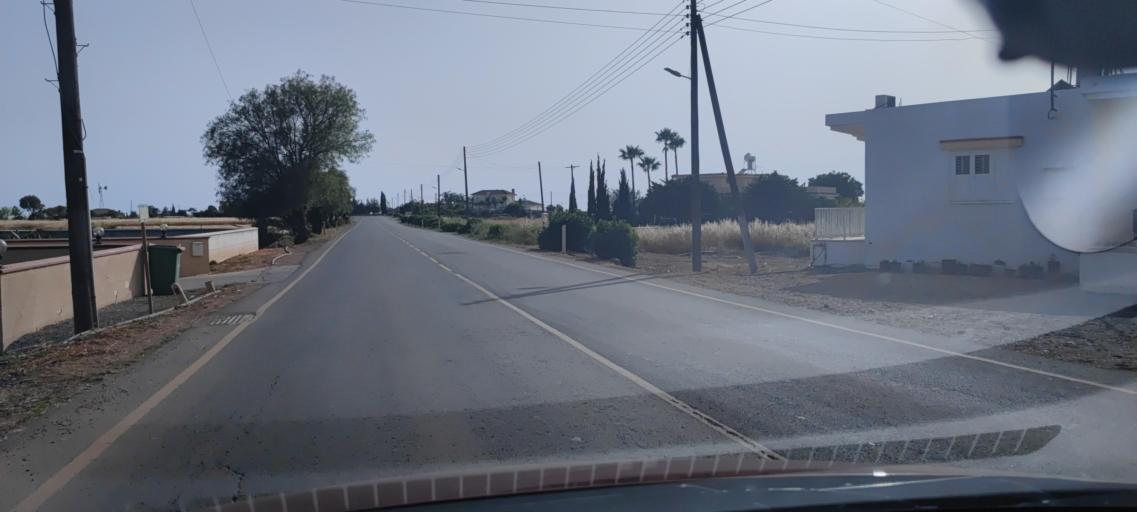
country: CY
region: Ammochostos
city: Frenaros
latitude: 35.0172
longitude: 33.9430
